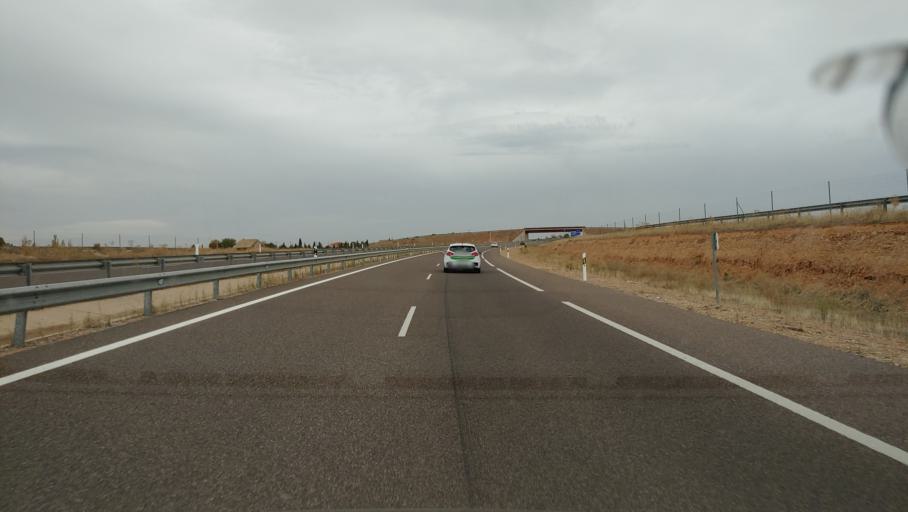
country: ES
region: Castille-La Mancha
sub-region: Provincia de Ciudad Real
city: Valenzuela de Calatrava
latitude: 38.8973
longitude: -3.8357
